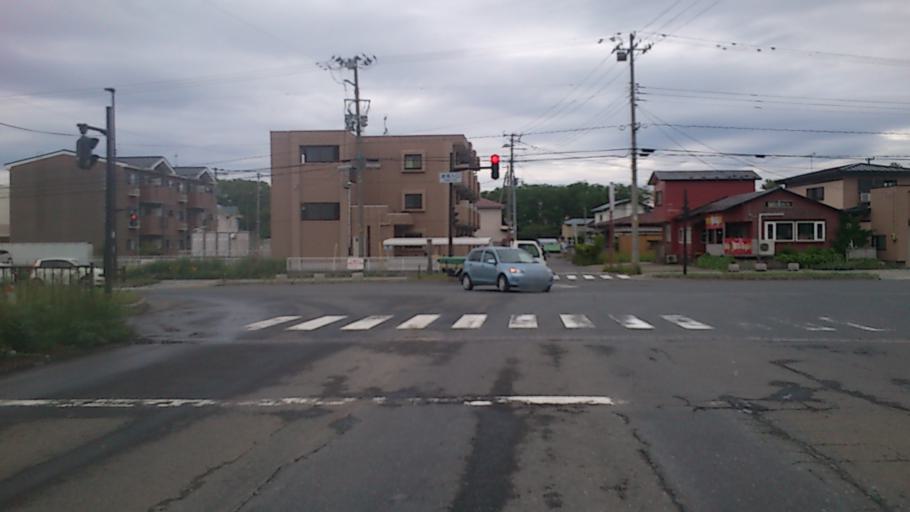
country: JP
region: Akita
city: Noshiromachi
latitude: 40.1874
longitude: 140.0123
